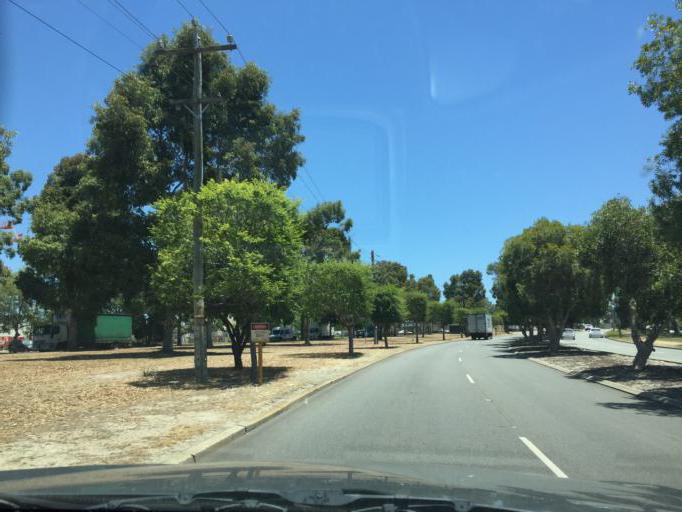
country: AU
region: Western Australia
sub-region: Canning
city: Canning Vale
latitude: -32.0627
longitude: 115.9245
